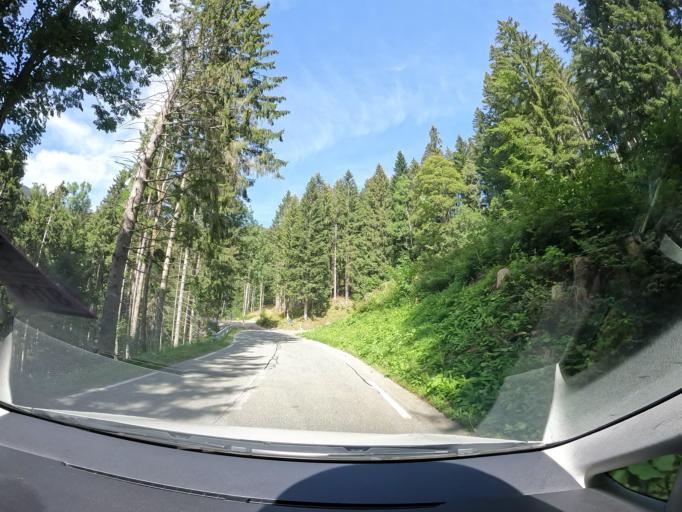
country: AT
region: Carinthia
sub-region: Politischer Bezirk Feldkirchen
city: Glanegg
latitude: 46.7462
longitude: 14.2158
